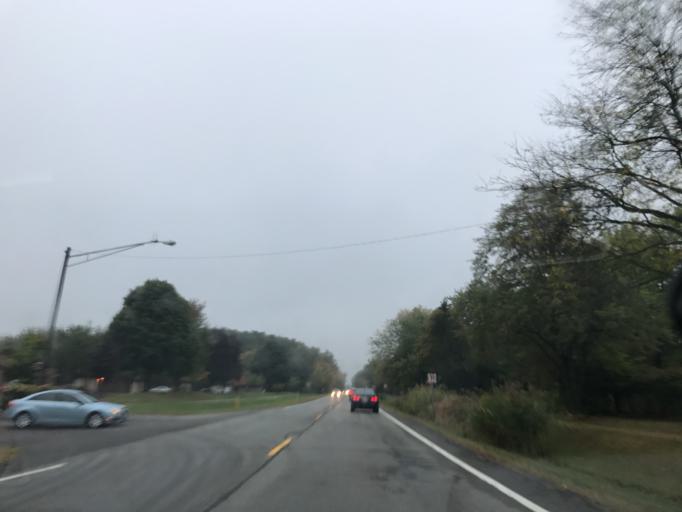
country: US
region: Michigan
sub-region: Oakland County
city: Franklin
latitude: 42.4820
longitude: -83.3188
